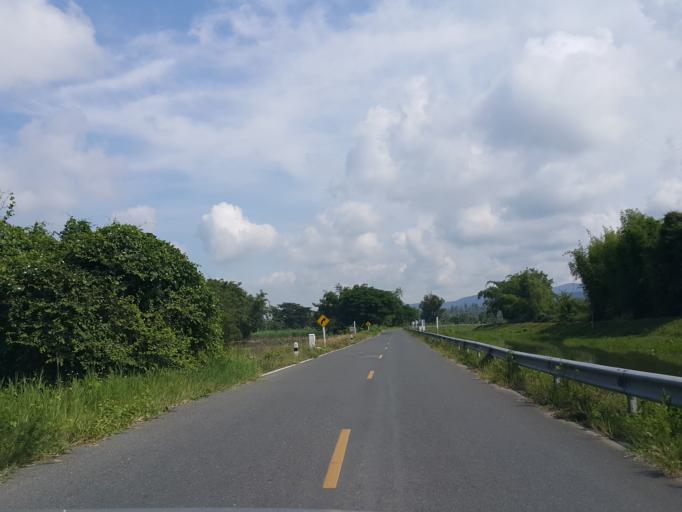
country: TH
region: Chiang Mai
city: San Sai
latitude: 18.9530
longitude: 98.9890
